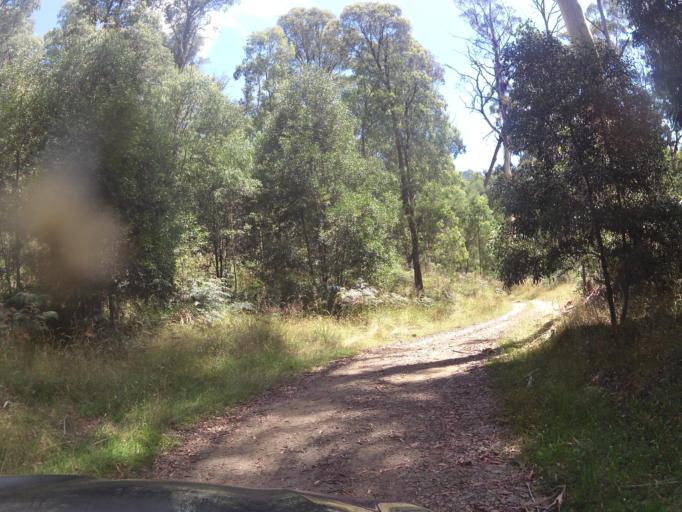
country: AU
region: Victoria
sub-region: Alpine
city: Mount Beauty
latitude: -36.8011
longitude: 147.0960
